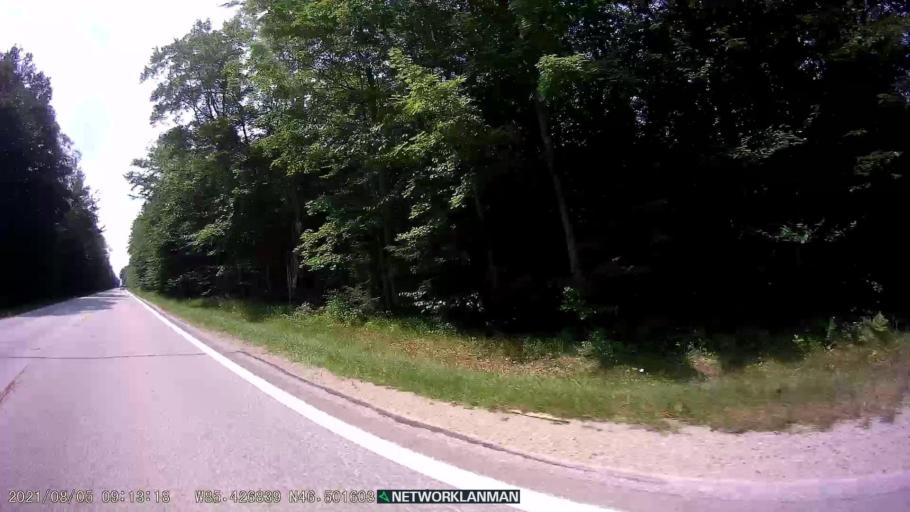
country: US
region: Michigan
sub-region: Luce County
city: Newberry
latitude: 46.5012
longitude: -85.4267
